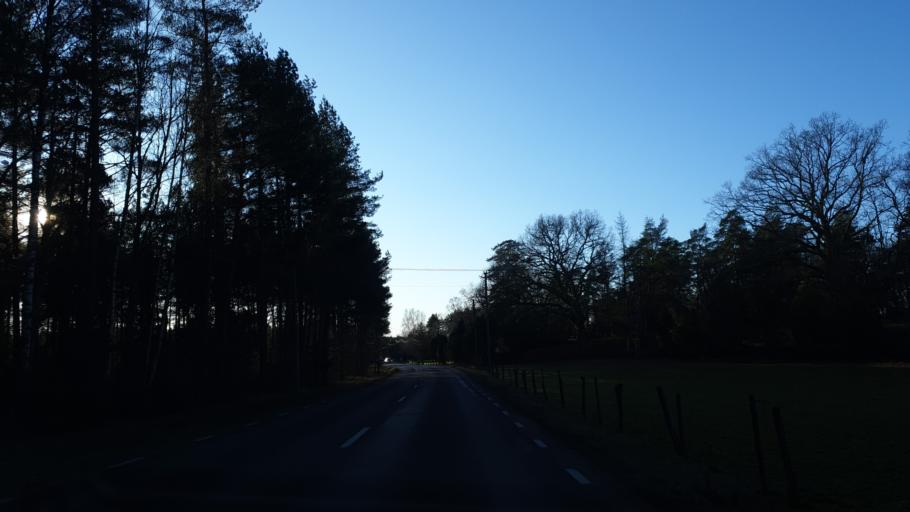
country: SE
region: Blekinge
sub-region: Ronneby Kommun
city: Kallinge
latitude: 56.2046
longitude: 15.3794
